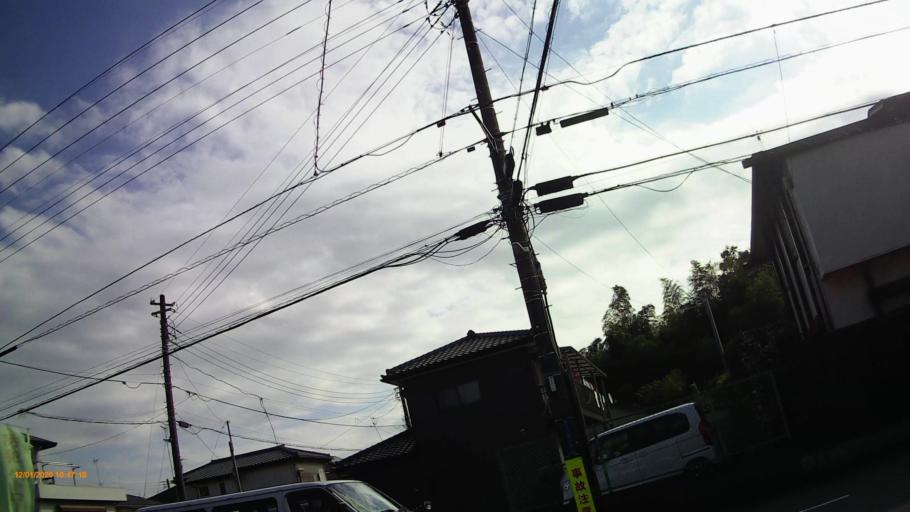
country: JP
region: Chiba
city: Yotsukaido
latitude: 35.6220
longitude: 140.1974
